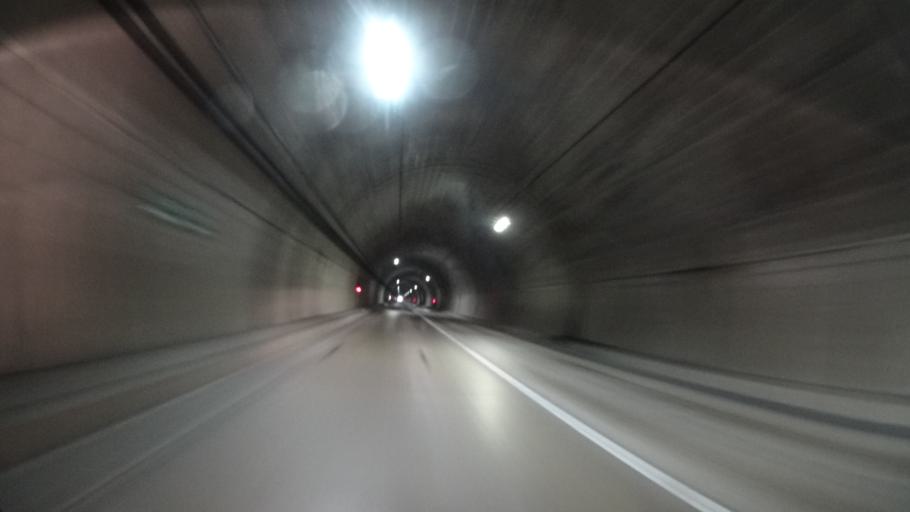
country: JP
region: Fukui
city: Maruoka
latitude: 36.1268
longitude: 136.3231
